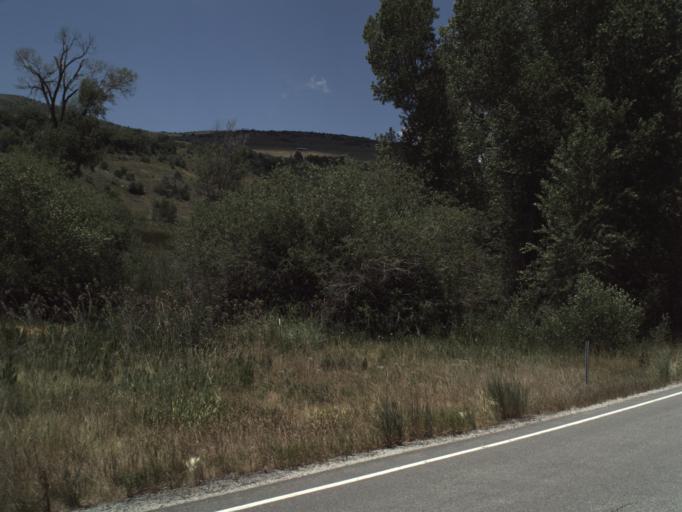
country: US
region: Utah
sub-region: Weber County
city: Wolf Creek
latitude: 41.3116
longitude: -111.6156
